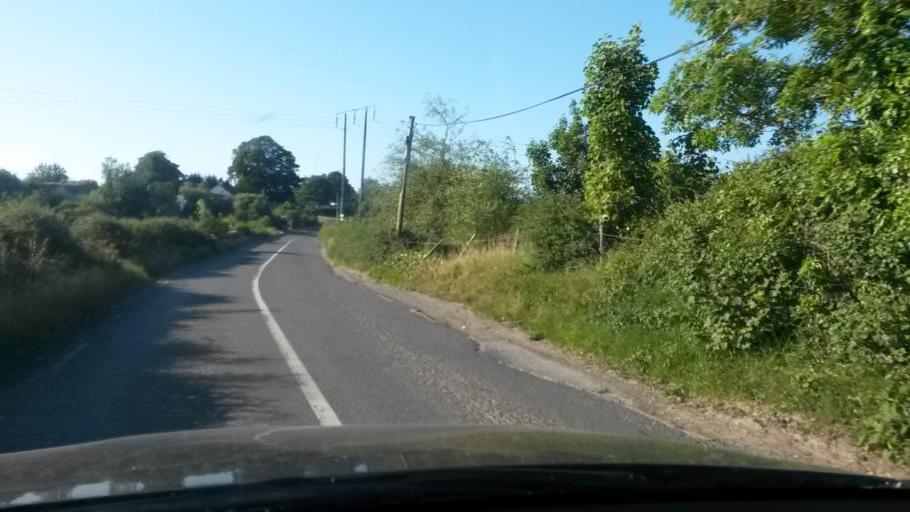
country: IE
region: Leinster
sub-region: Dublin City
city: Finglas
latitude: 53.4536
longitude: -6.3096
